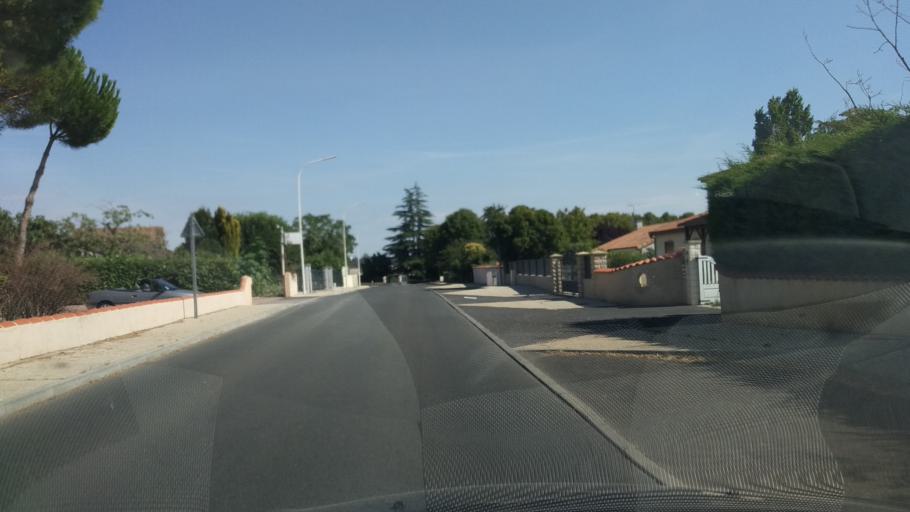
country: FR
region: Poitou-Charentes
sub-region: Departement de la Vienne
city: Cisse
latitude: 46.6482
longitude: 0.2252
